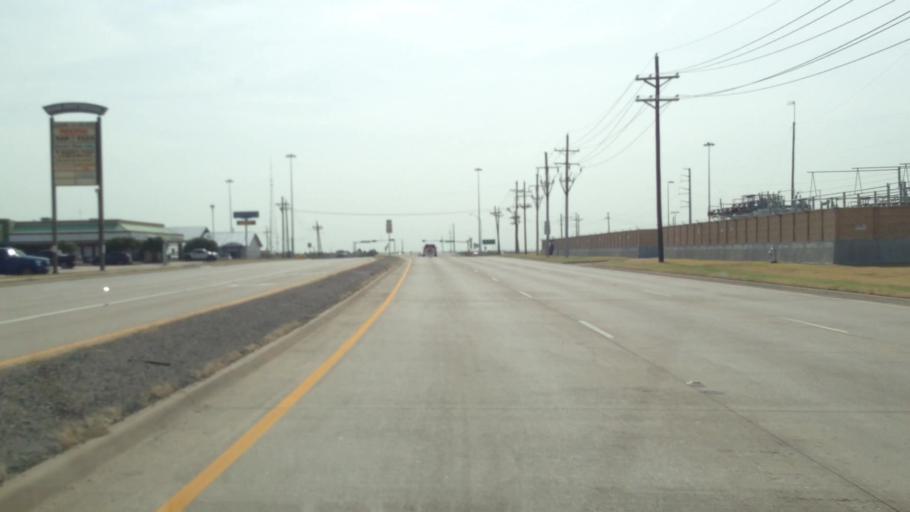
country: US
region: Texas
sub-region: Denton County
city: Lewisville
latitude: 33.0035
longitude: -96.9981
